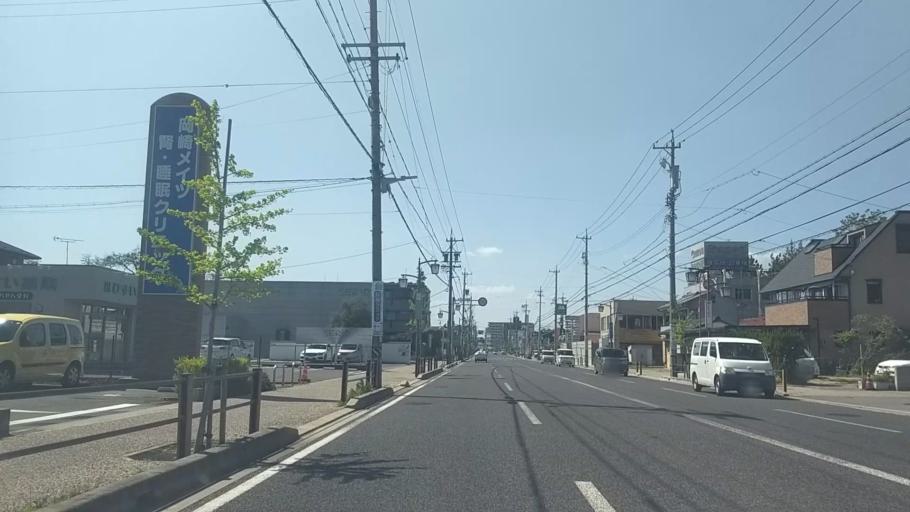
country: JP
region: Aichi
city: Okazaki
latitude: 34.9693
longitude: 137.1751
